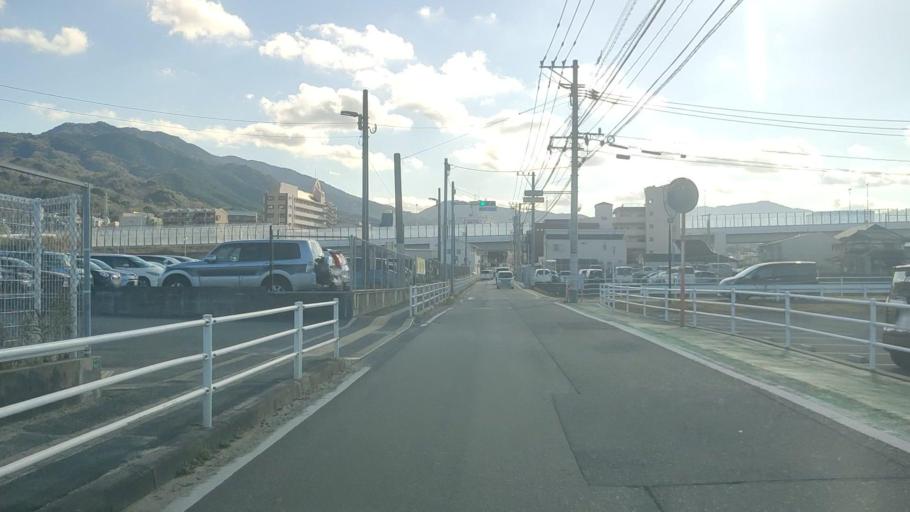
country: JP
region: Fukuoka
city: Fukuoka-shi
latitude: 33.5474
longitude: 130.3571
